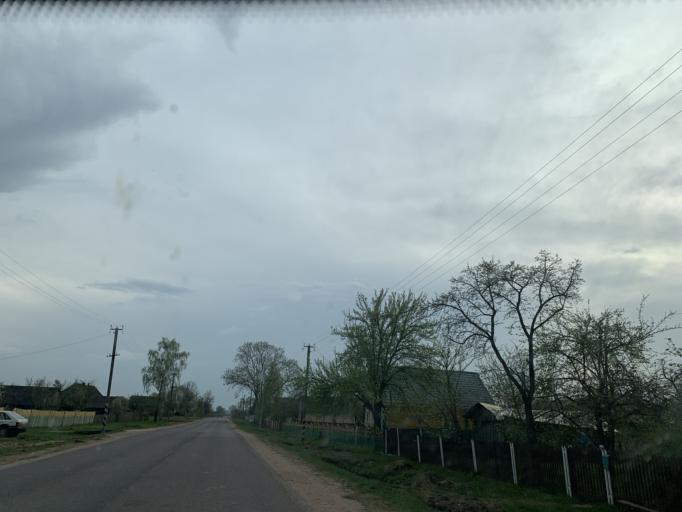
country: BY
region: Minsk
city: Kapyl'
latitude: 53.2831
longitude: 26.9809
